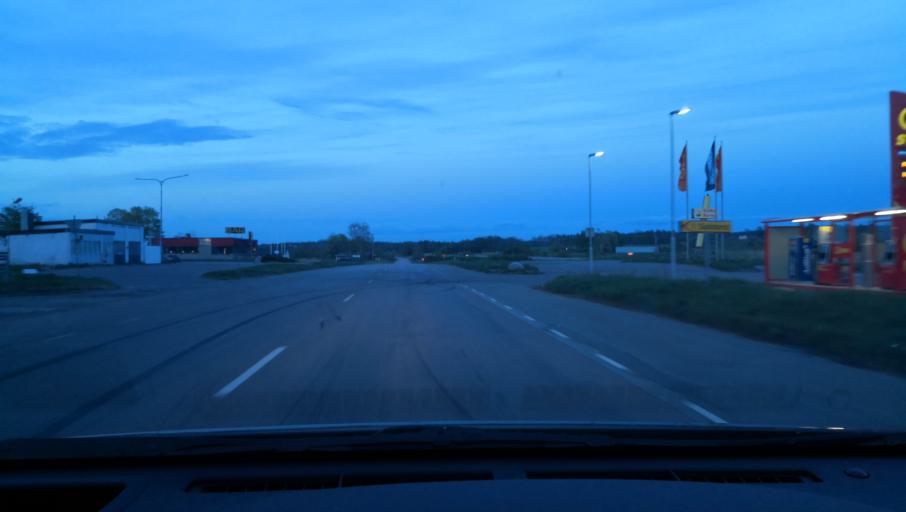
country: SE
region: OErebro
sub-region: Lekebergs Kommun
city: Fjugesta
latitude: 59.0375
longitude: 14.8974
